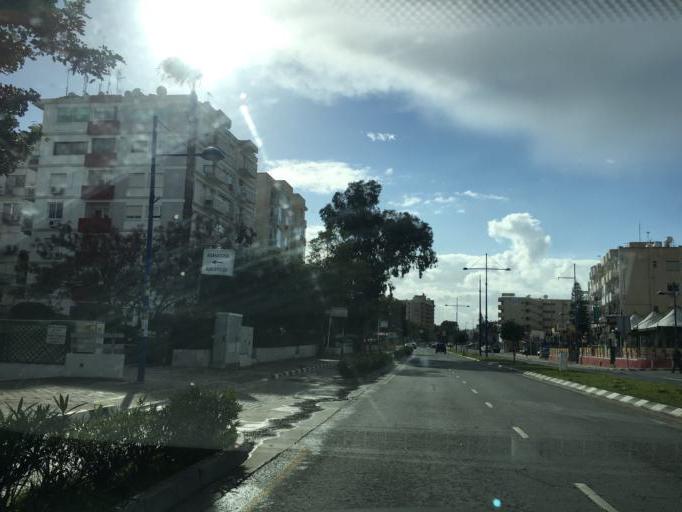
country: CY
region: Limassol
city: Mouttagiaka
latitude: 34.7071
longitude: 33.1204
